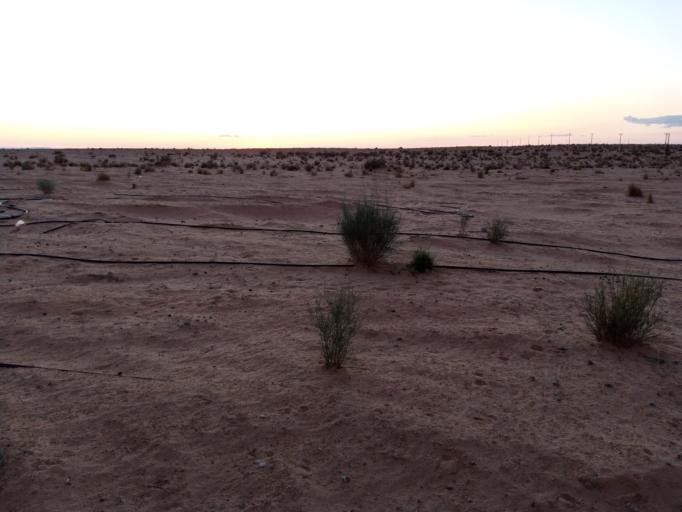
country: LY
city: Giado
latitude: 32.0898
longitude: 11.6390
